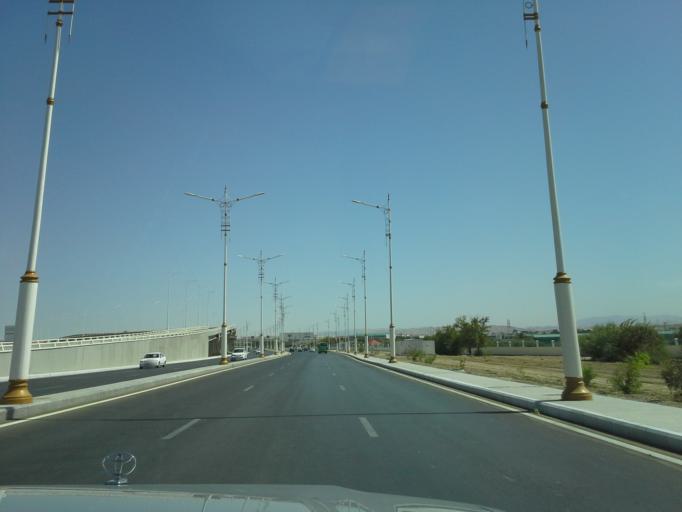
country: TM
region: Ahal
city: Ashgabat
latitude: 37.9306
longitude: 58.4191
